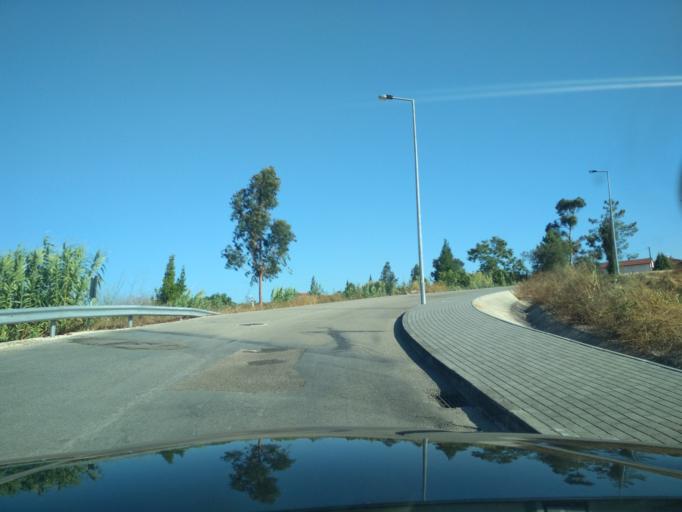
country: PT
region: Coimbra
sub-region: Condeixa-A-Nova
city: Condeixa-a-Nova
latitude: 40.1118
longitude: -8.5073
